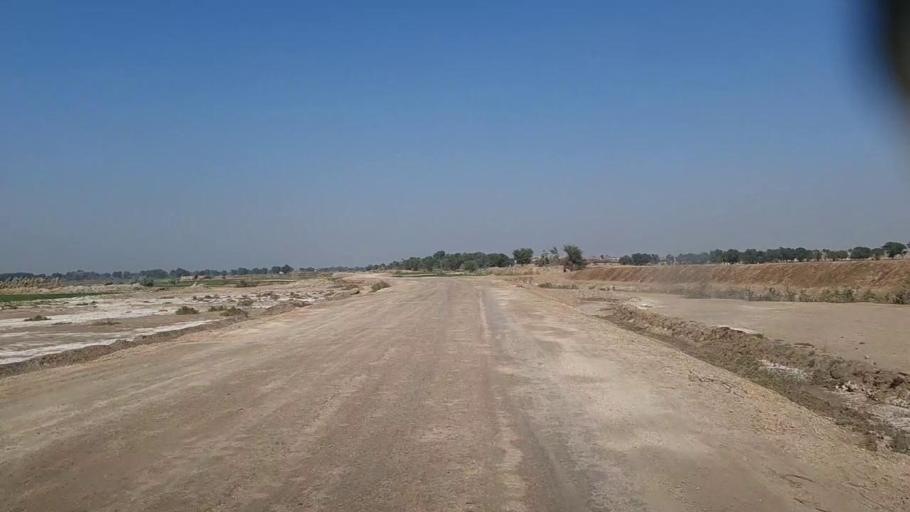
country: PK
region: Sindh
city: Khairpur
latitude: 27.9827
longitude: 69.8496
